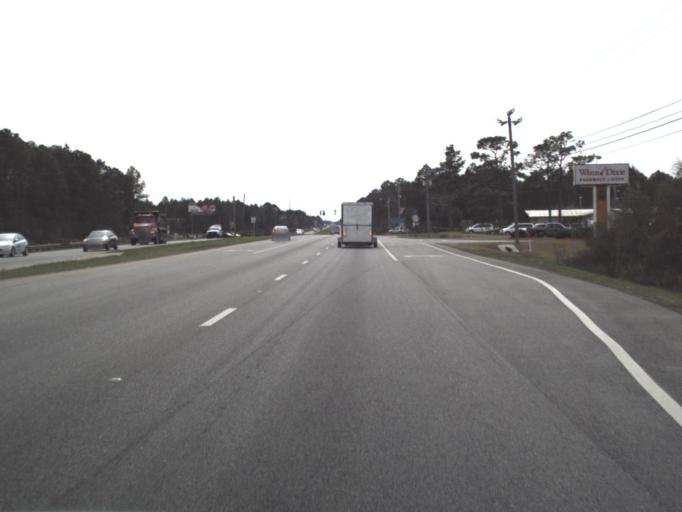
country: US
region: Florida
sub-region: Bay County
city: Hiland Park
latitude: 30.2148
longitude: -85.6053
